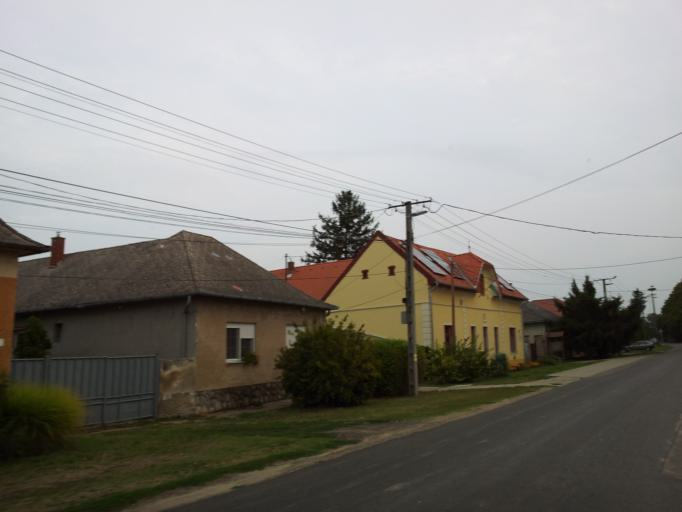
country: HU
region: Tolna
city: Szentgalpuszta
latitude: 46.3900
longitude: 18.6492
